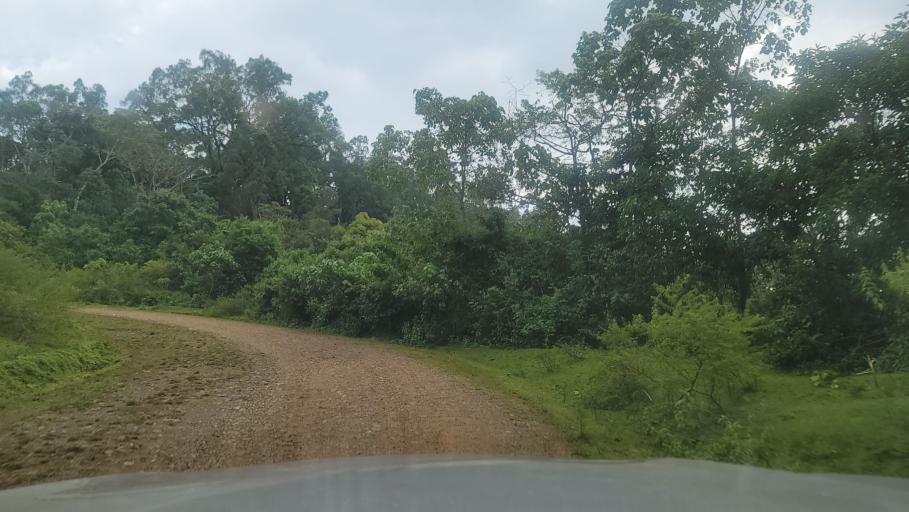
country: ET
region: Southern Nations, Nationalities, and People's Region
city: Bonga
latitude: 7.6818
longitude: 36.2404
